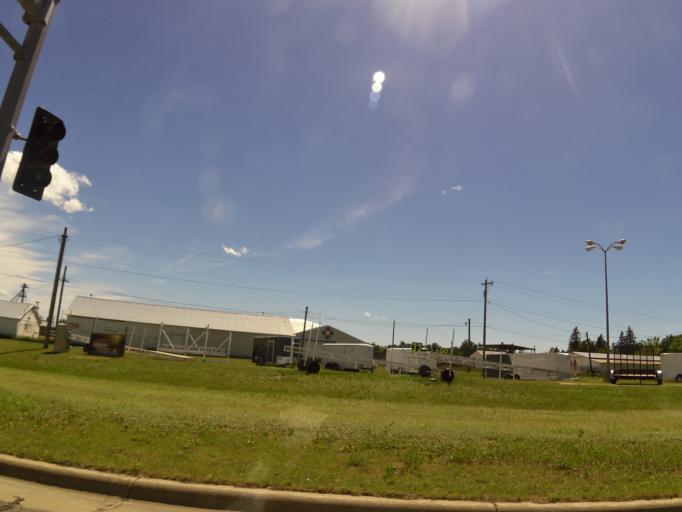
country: US
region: Minnesota
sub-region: Todd County
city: Staples
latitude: 46.3403
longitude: -94.6469
